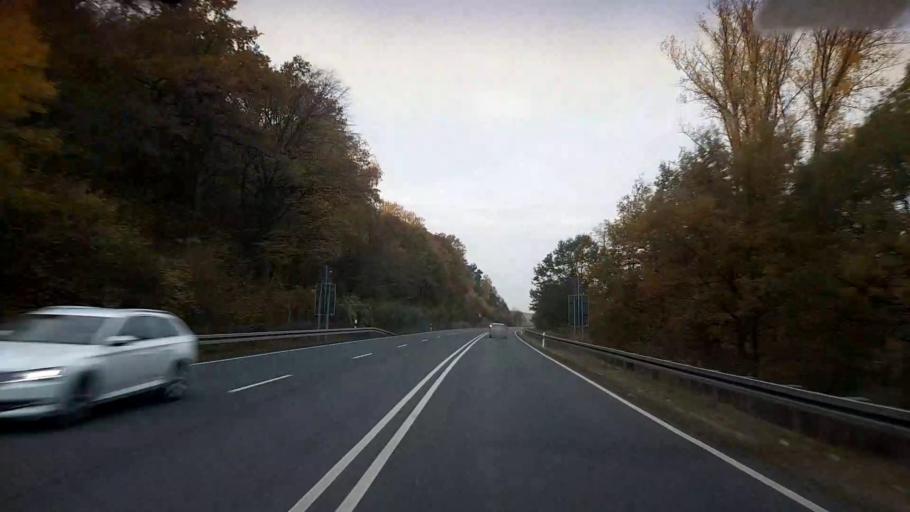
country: DE
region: Bavaria
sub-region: Upper Franconia
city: Strullendorf
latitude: 49.8213
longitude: 10.9580
